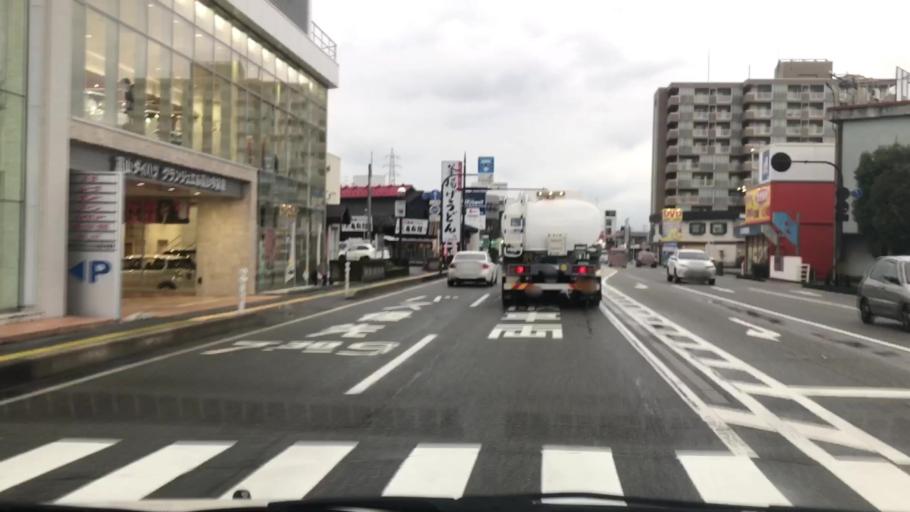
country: JP
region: Toyama
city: Toyama-shi
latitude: 36.6714
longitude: 137.2104
